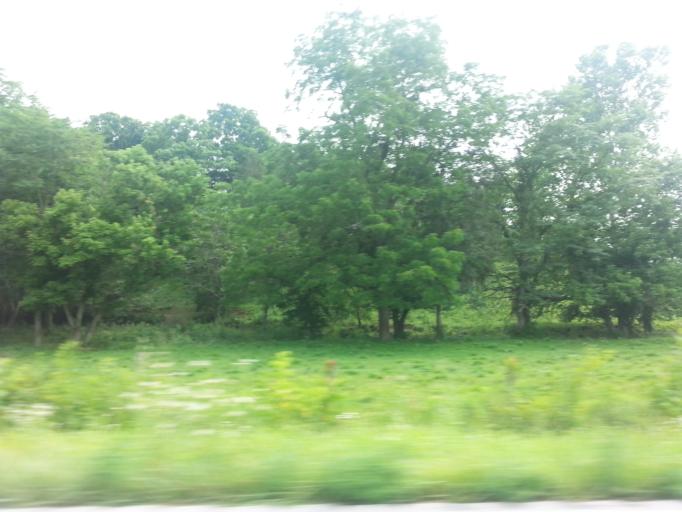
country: US
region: Kentucky
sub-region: Robertson County
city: Mount Olivet
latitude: 38.5192
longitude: -84.1597
